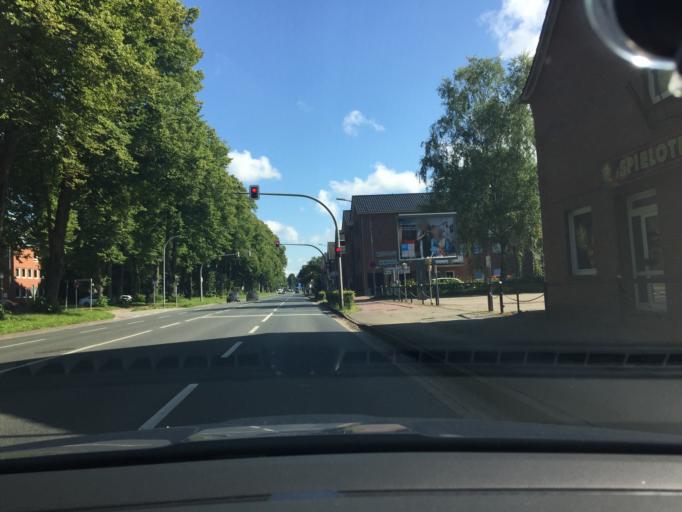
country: DE
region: Lower Saxony
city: Aurich
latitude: 53.4769
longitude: 7.4862
